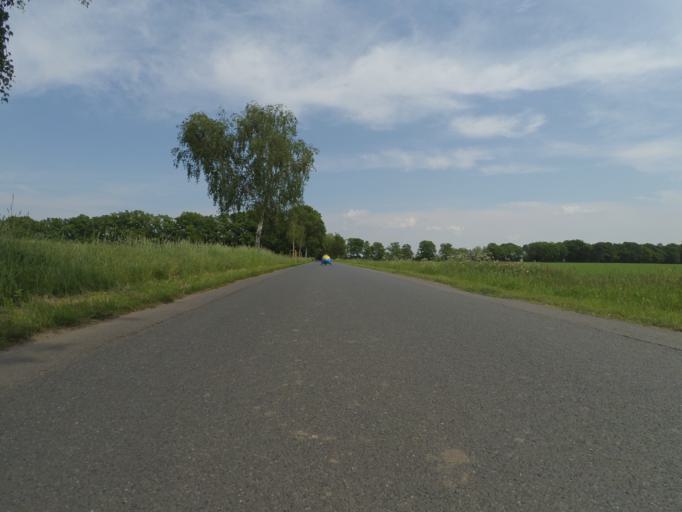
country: DE
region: Lower Saxony
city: Arpke
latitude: 52.3529
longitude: 10.1342
